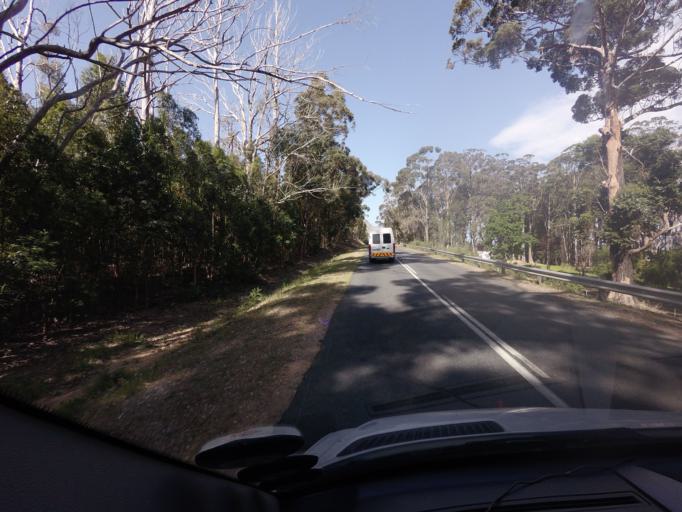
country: ZA
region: Western Cape
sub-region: Overberg District Municipality
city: Hermanus
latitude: -34.4051
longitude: 19.3632
